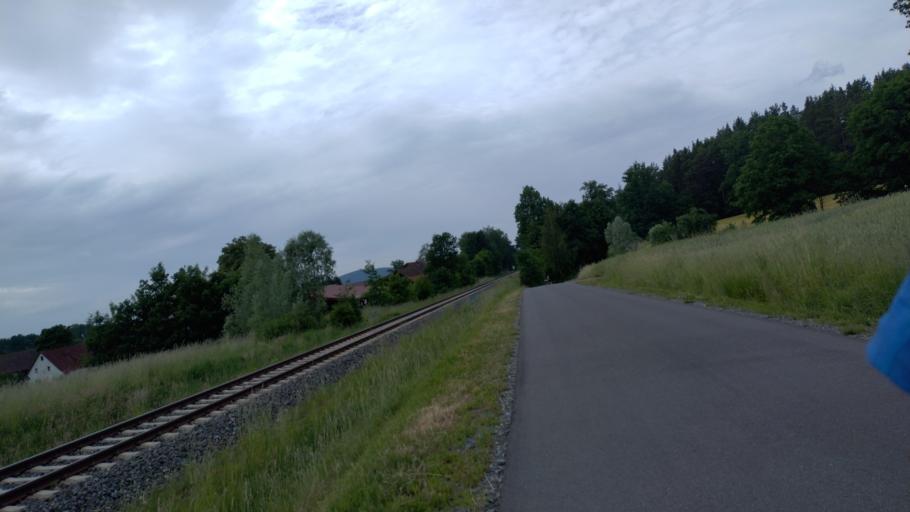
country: DE
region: Bavaria
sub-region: Upper Franconia
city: Harsdorf
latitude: 50.0157
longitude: 11.5795
